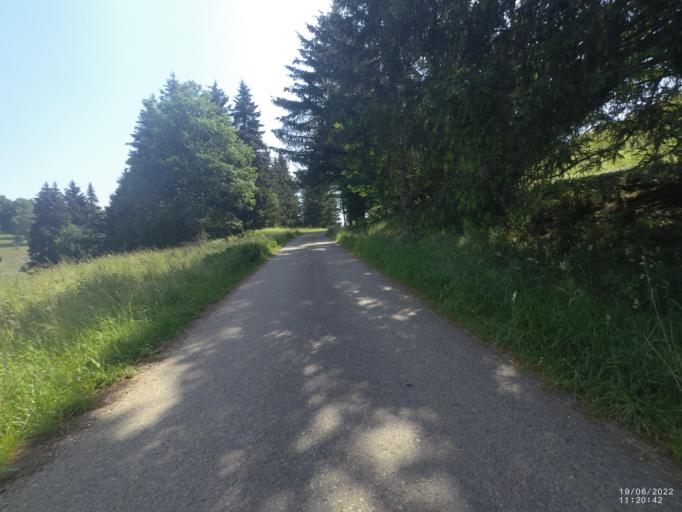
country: DE
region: Baden-Wuerttemberg
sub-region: Tuebingen Region
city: Weidenstetten
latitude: 48.6094
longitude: 9.9777
